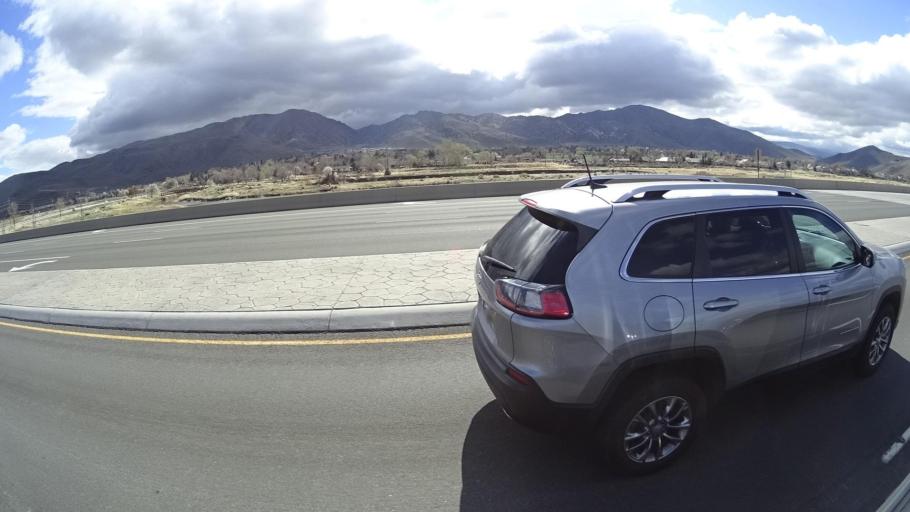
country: US
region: Nevada
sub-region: Washoe County
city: Sparks
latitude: 39.4972
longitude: -119.7302
